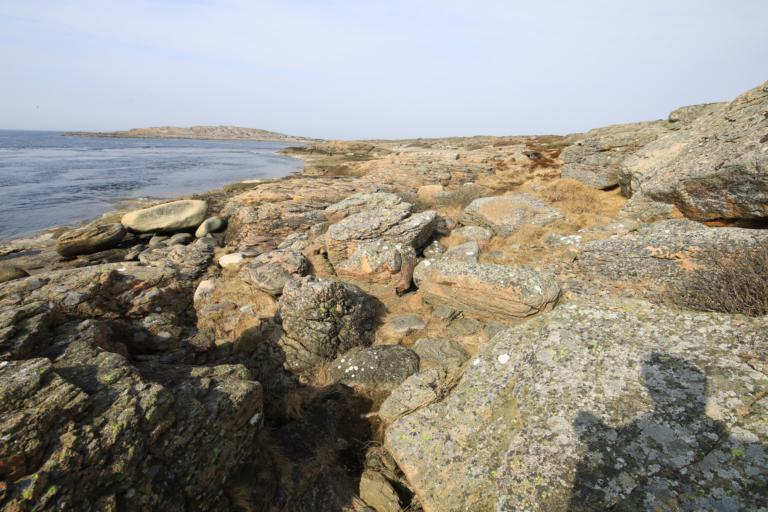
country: SE
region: Halland
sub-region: Kungsbacka Kommun
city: Frillesas
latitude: 57.2517
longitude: 12.0910
